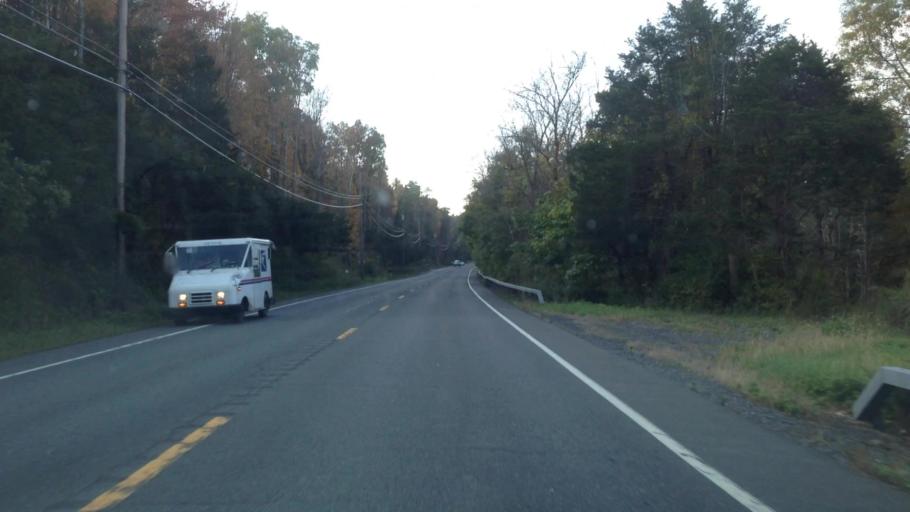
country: US
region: New York
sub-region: Ulster County
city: Tillson
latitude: 41.7882
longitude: -74.0695
